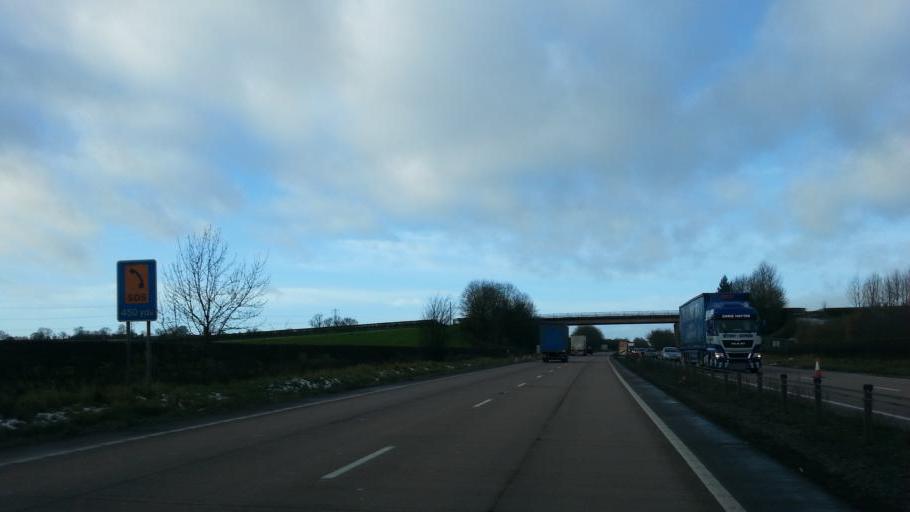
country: GB
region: England
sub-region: Staffordshire
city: Uttoxeter
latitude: 52.9143
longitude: -1.9013
